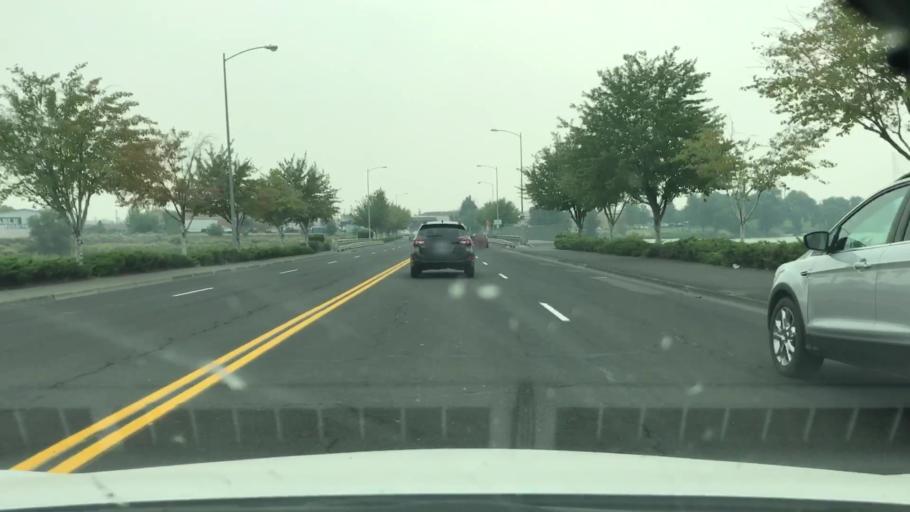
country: US
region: Washington
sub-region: Grant County
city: Moses Lake
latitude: 47.1350
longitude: -119.2785
